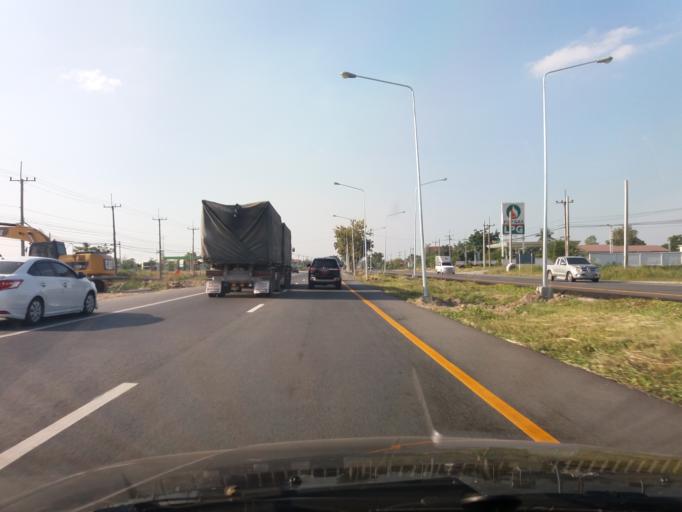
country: TH
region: Nakhon Sawan
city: Banphot Phisai
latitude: 15.8169
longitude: 99.9425
